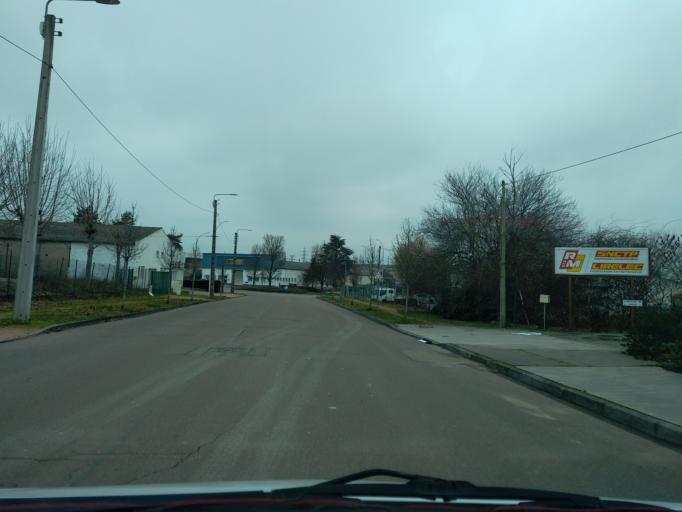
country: FR
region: Bourgogne
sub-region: Departement de la Cote-d'Or
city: Saint-Apollinaire
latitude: 47.3474
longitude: 5.0656
